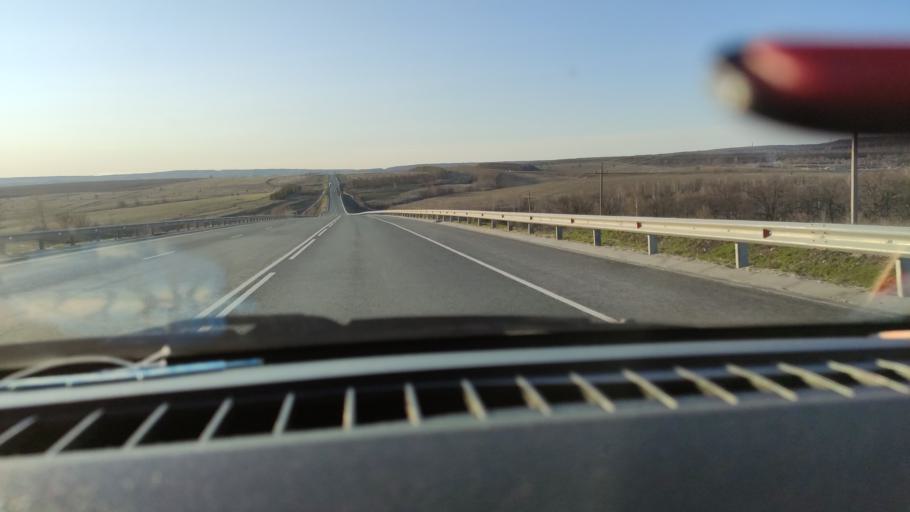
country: RU
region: Saratov
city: Shikhany
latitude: 52.1413
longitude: 47.2072
